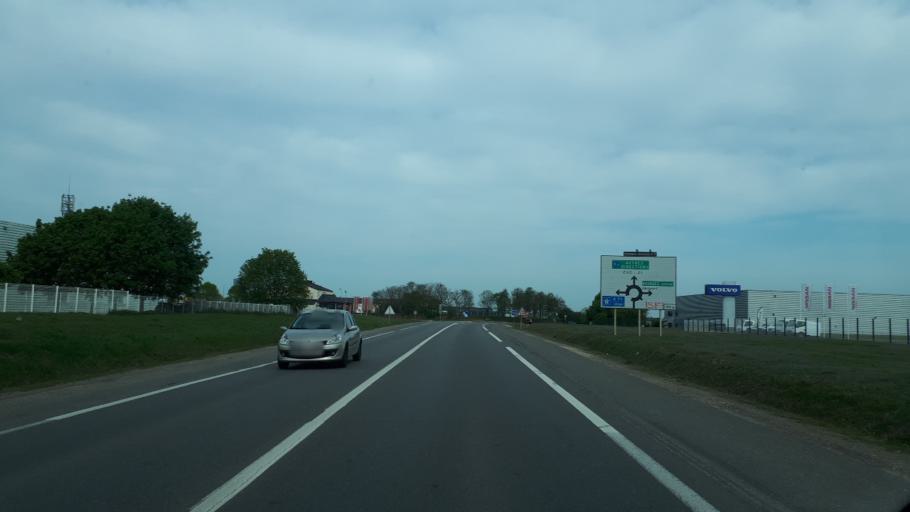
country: FR
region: Centre
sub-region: Departement du Cher
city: La Chapelle-Saint-Ursin
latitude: 47.0448
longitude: 2.3465
